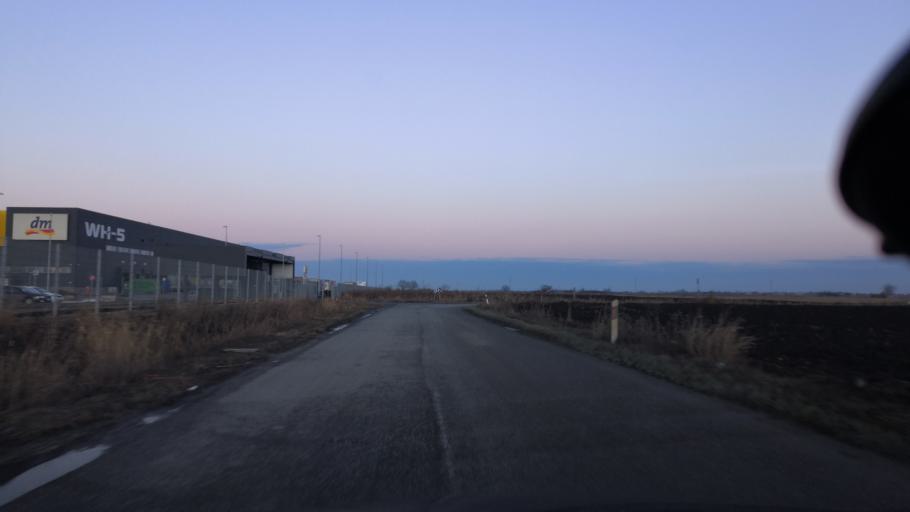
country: RS
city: Simanovci
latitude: 44.8910
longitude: 20.1077
